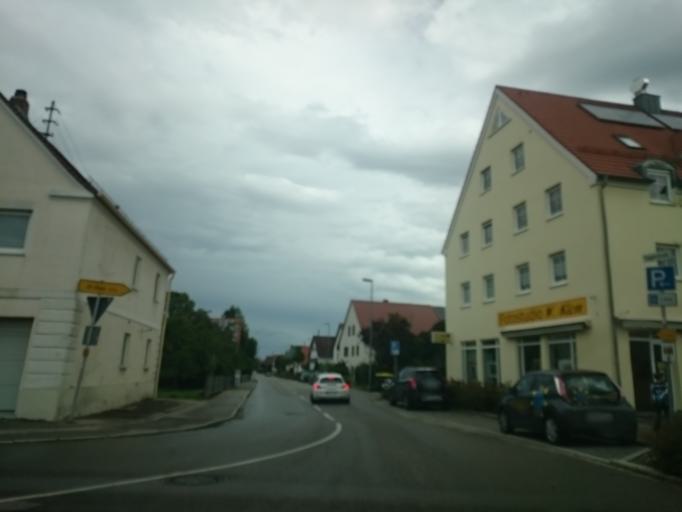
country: DE
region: Bavaria
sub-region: Swabia
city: Untermeitingen
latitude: 48.1621
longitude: 10.8074
